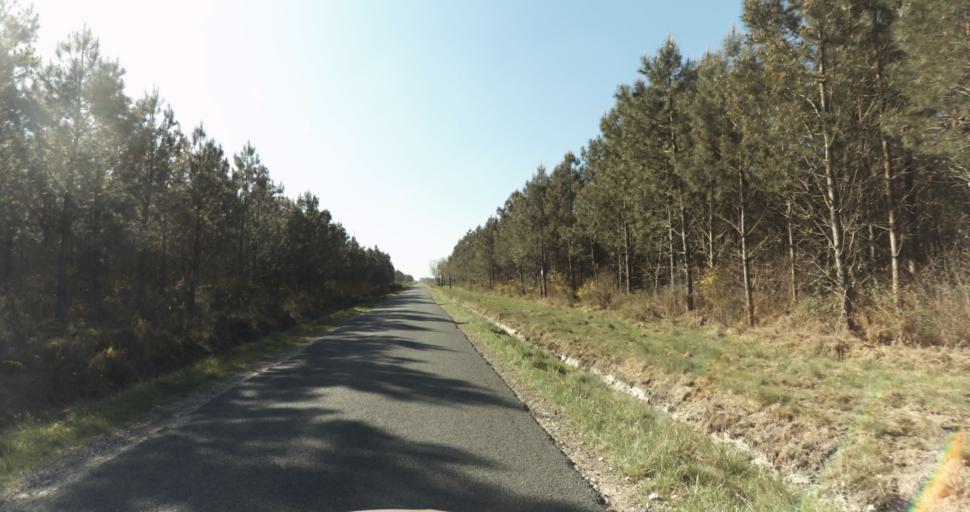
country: FR
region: Aquitaine
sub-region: Departement de la Gironde
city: Marcheprime
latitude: 44.7855
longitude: -0.8623
